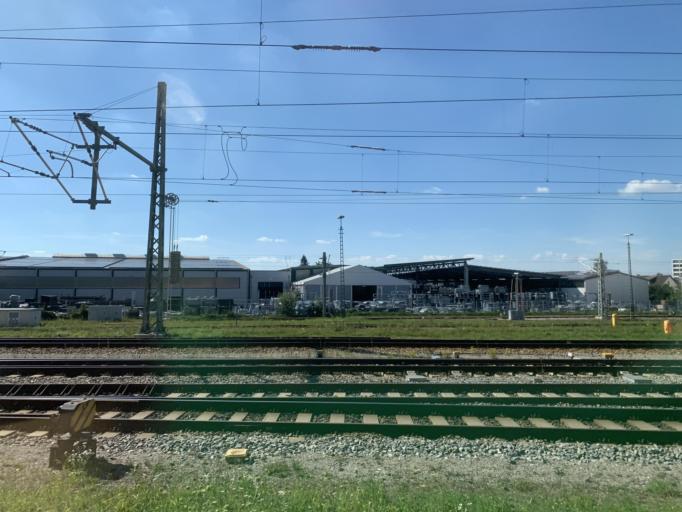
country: DE
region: Bavaria
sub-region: Swabia
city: Buchloe
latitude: 48.0301
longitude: 10.7141
